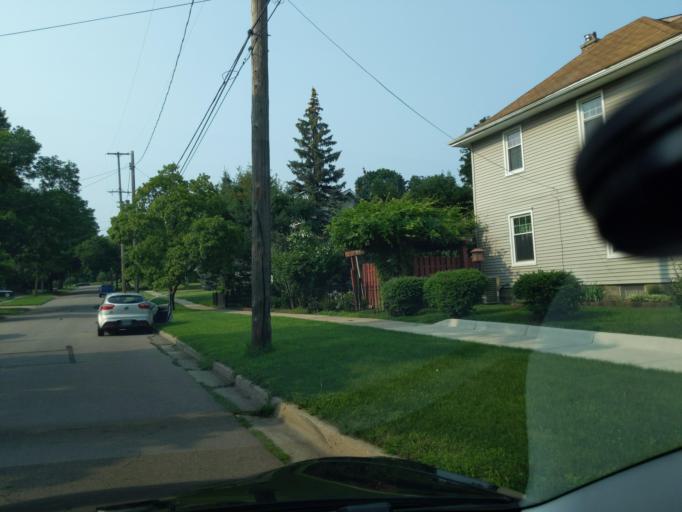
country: US
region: Michigan
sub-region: Jackson County
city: Jackson
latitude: 42.2457
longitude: -84.4246
